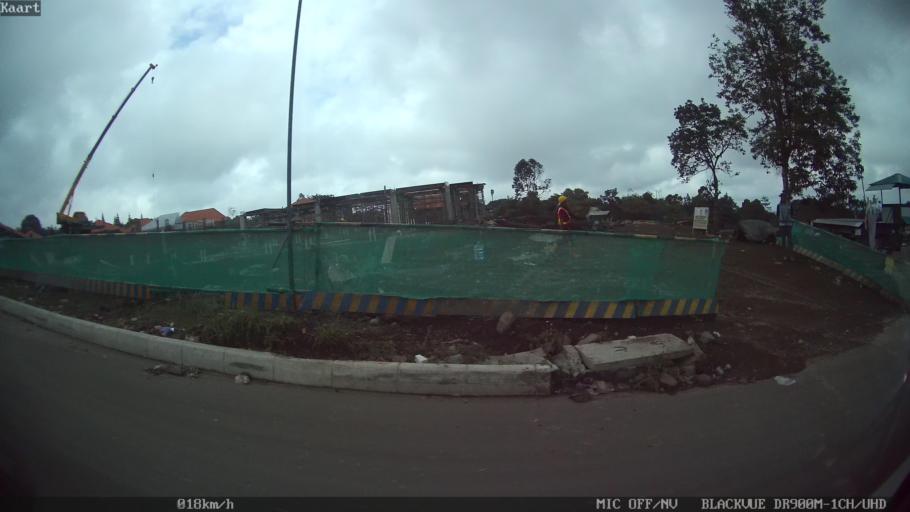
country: ID
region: Bali
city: Banjar Bias
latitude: -8.3745
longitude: 115.4486
